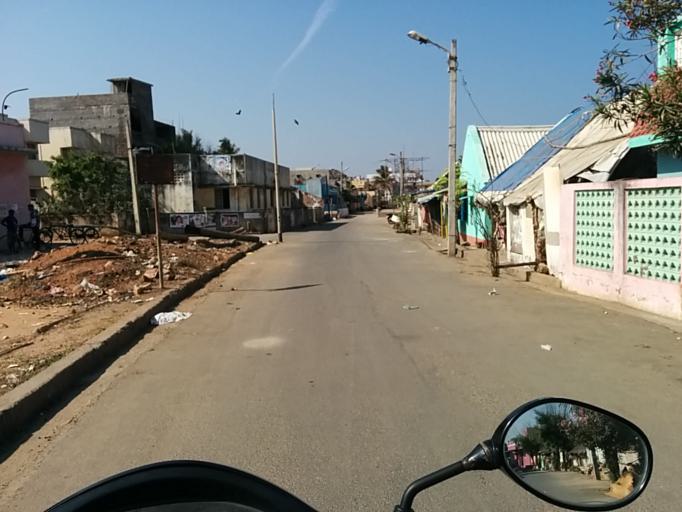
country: IN
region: Pondicherry
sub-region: Puducherry
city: Puducherry
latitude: 11.9430
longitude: 79.8372
